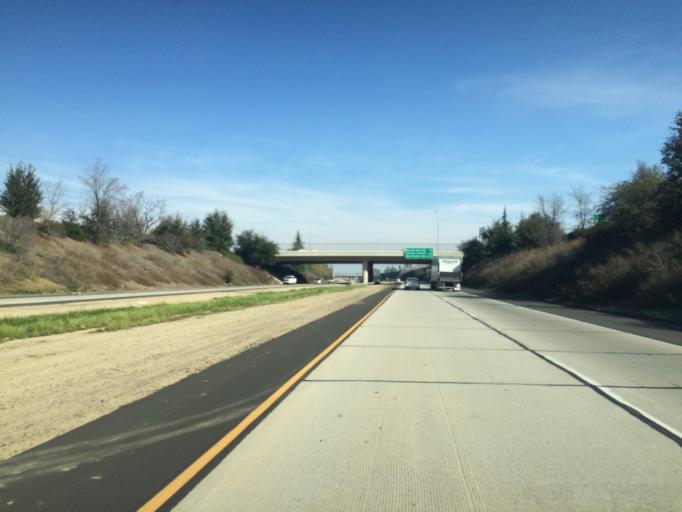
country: US
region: California
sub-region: Tulare County
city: Visalia
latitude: 36.3272
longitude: -119.3337
